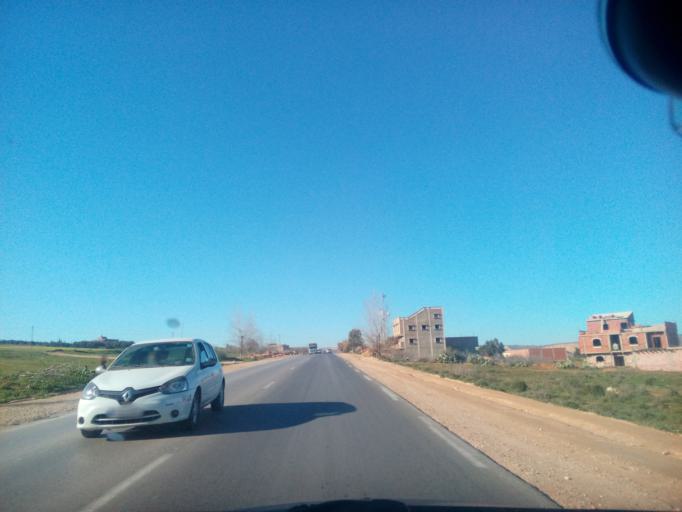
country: DZ
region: Relizane
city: Relizane
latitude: 35.9080
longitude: 0.5090
